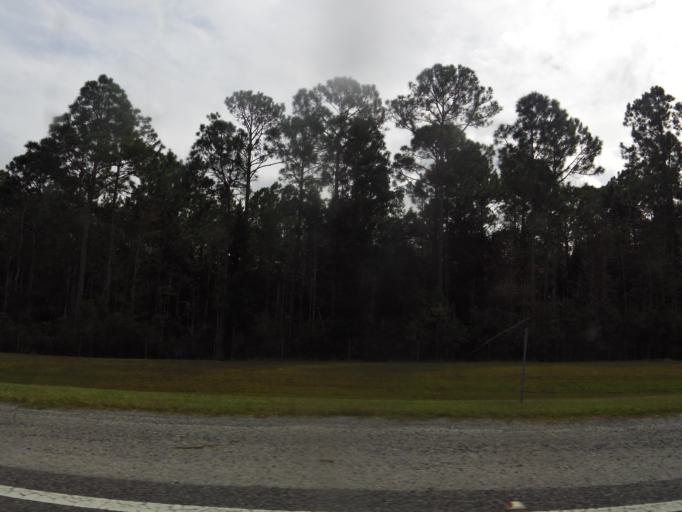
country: US
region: Florida
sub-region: Saint Johns County
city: Palm Valley
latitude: 30.1093
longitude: -81.4436
